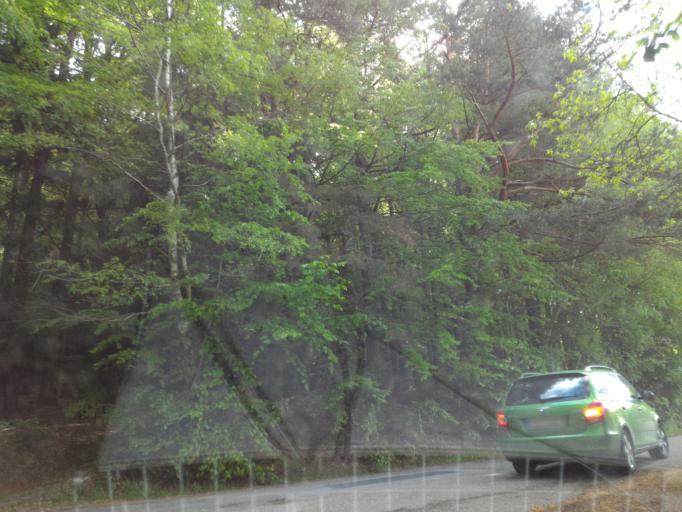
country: CZ
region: Vysocina
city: Ledec nad Sazavou
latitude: 49.6316
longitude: 15.3059
